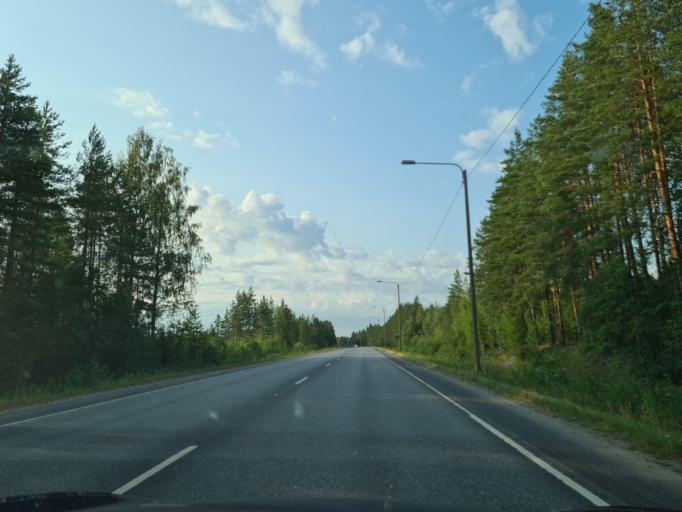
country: FI
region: Southern Ostrobothnia
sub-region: Seinaejoki
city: Kauhava
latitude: 63.0467
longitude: 23.0386
